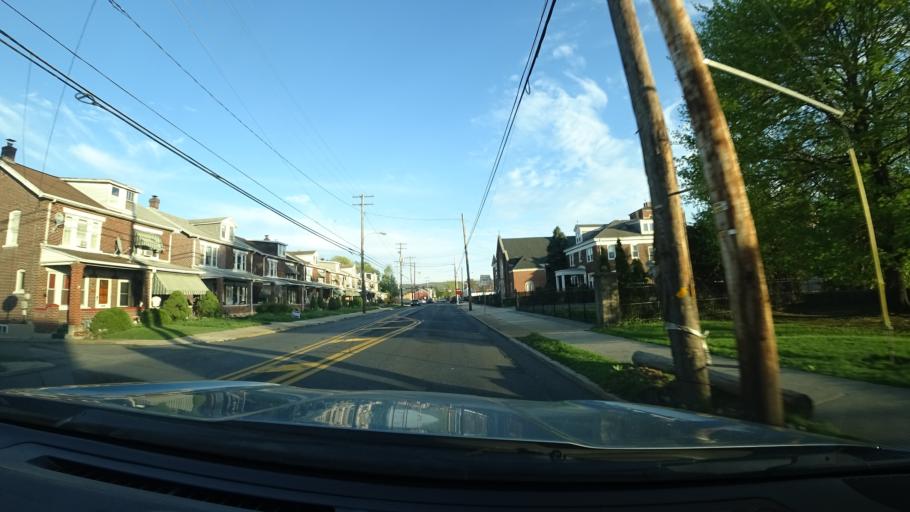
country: US
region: Pennsylvania
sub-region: Lehigh County
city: Fullerton
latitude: 40.6195
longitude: -75.4622
